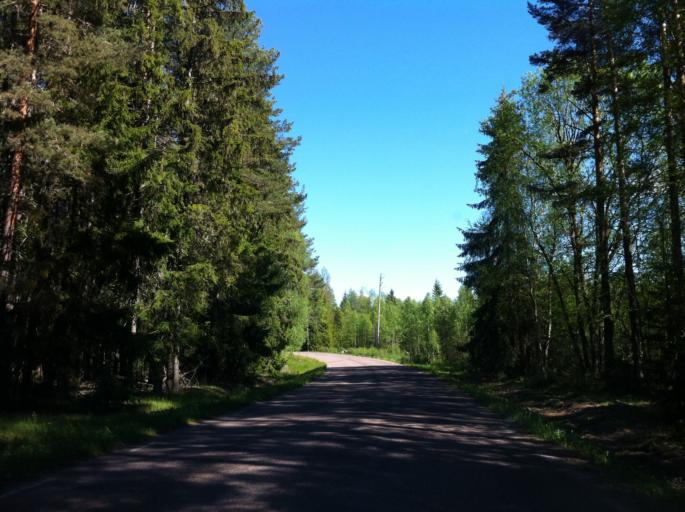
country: SE
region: Dalarna
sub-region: Mora Kommun
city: Mora
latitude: 60.9604
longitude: 14.6619
